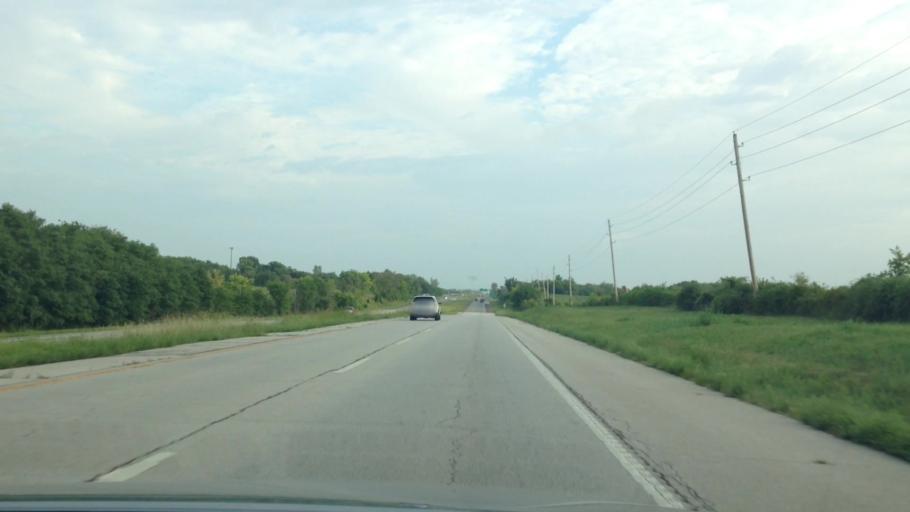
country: US
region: Missouri
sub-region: Clay County
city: Smithville
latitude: 39.3247
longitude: -94.5845
